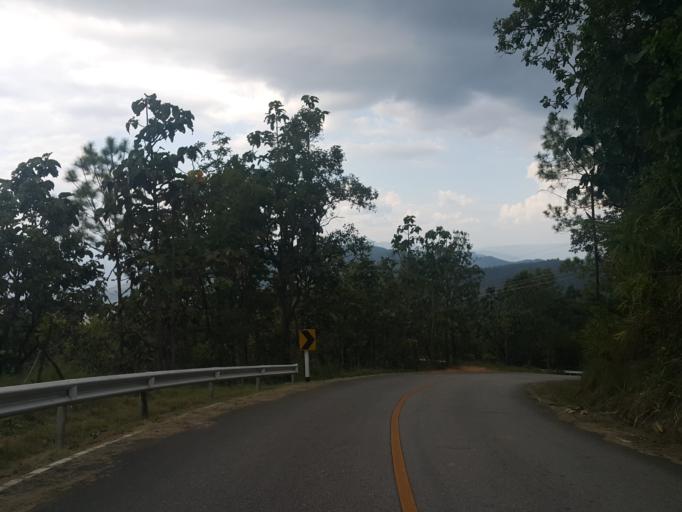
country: TH
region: Chiang Mai
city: Mae Chaem
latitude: 18.5086
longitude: 98.4381
